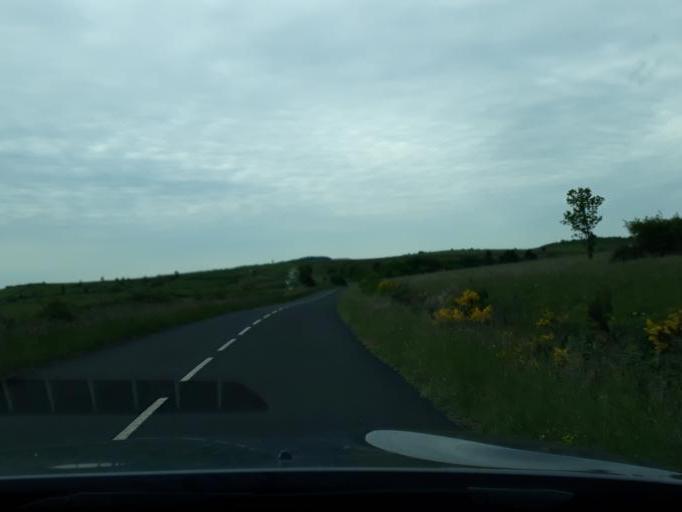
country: FR
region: Languedoc-Roussillon
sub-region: Departement de l'Herault
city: Lodeve
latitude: 43.8333
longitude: 3.2500
